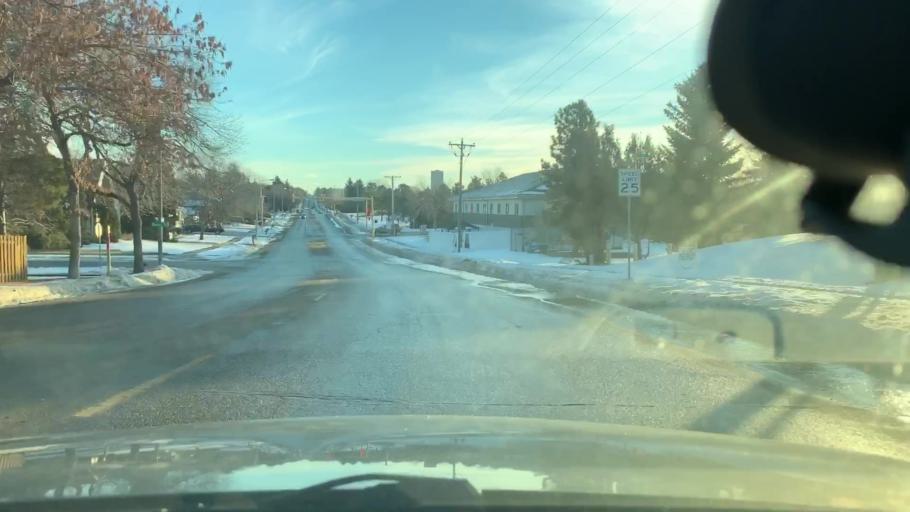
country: US
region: North Dakota
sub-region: Burleigh County
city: Bismarck
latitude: 46.8236
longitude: -100.8082
